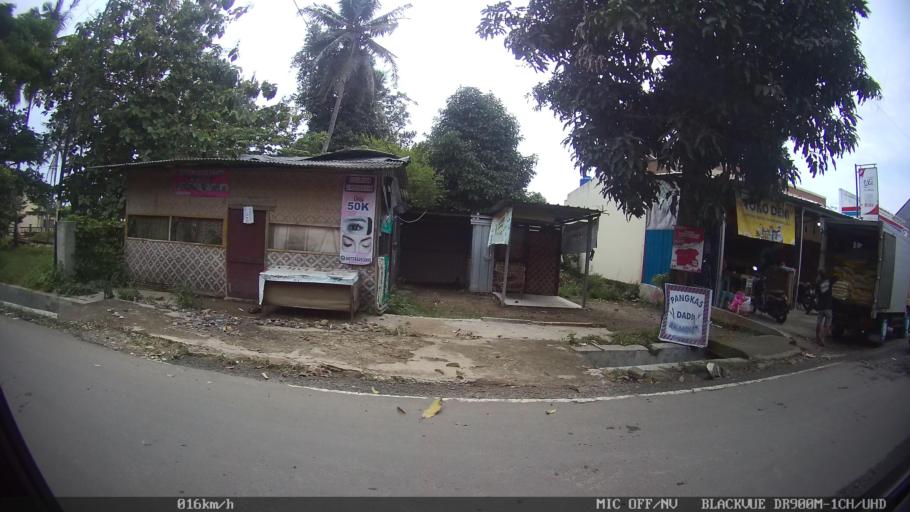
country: ID
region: Lampung
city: Kedaton
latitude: -5.3747
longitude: 105.2181
